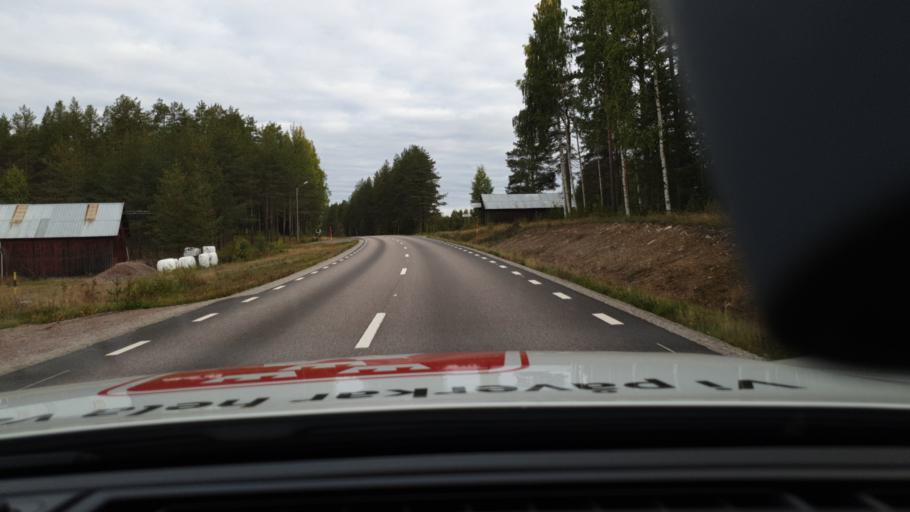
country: SE
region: Norrbotten
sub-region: Overkalix Kommun
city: OEverkalix
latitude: 66.4340
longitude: 22.7940
